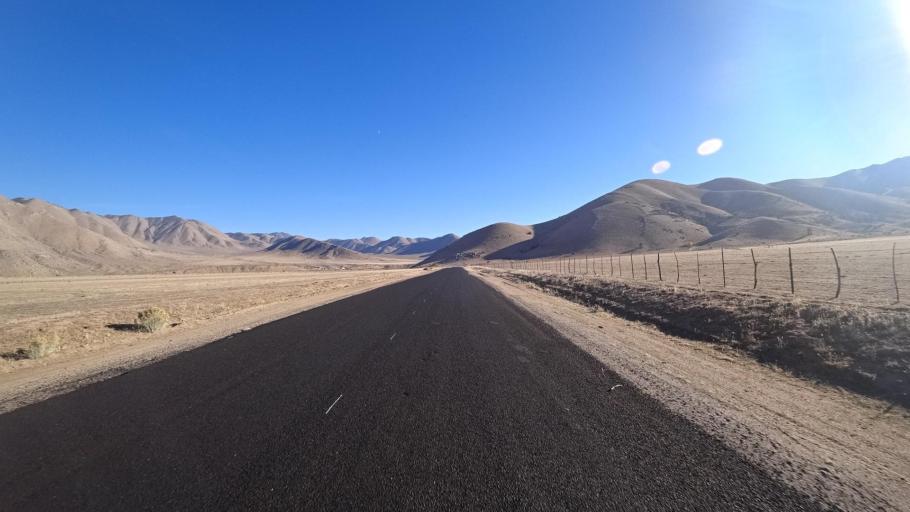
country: US
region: California
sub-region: Kern County
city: Weldon
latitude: 35.6225
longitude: -118.2586
